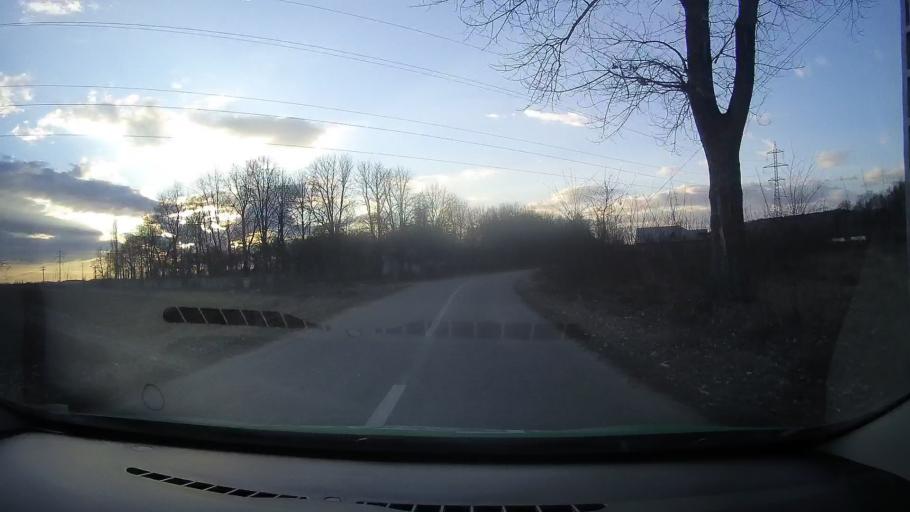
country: RO
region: Dambovita
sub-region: Comuna Gura Ocnitei
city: Gura Ocnitei
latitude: 44.9365
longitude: 25.5859
